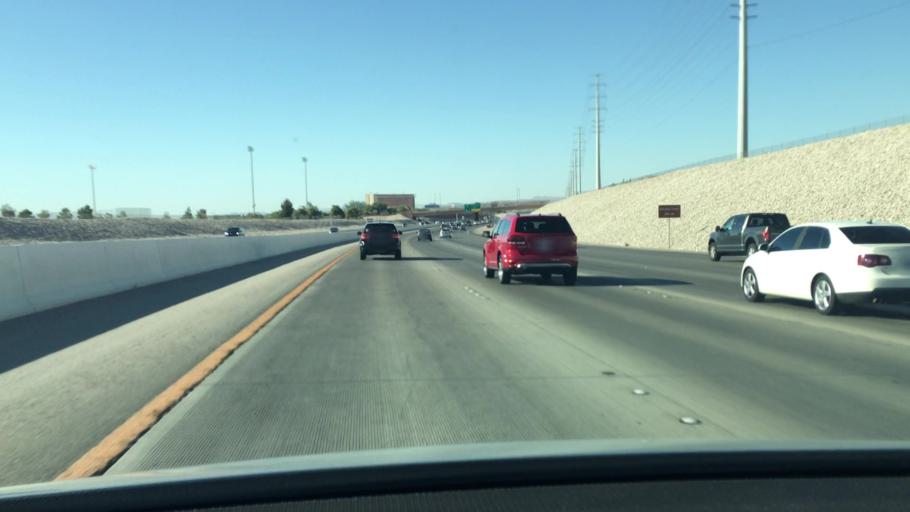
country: US
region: Nevada
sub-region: Clark County
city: Summerlin South
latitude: 36.1749
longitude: -115.3384
